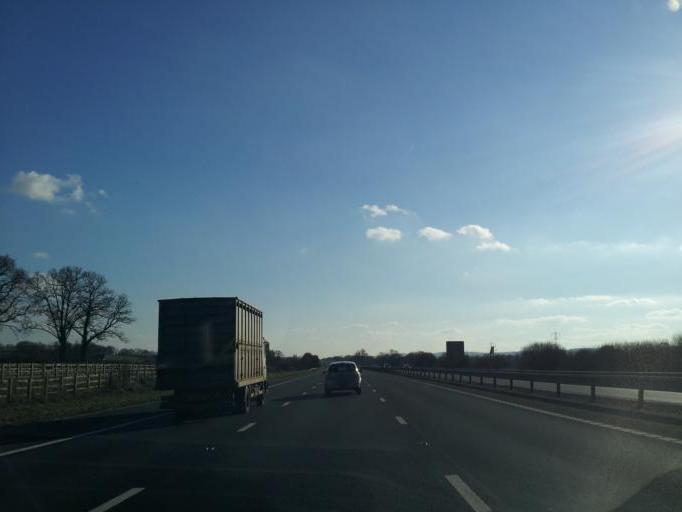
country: GB
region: England
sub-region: Devon
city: Uffculme
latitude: 50.9076
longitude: -3.3662
